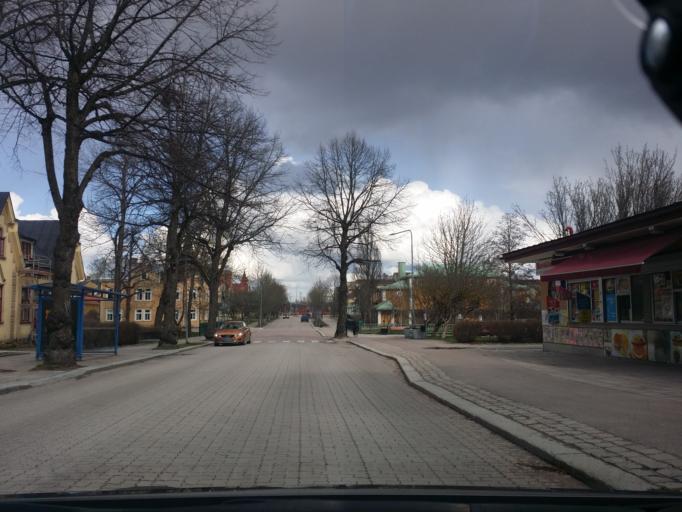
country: SE
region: Vaestmanland
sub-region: Sala Kommun
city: Sala
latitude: 59.9218
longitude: 16.6082
